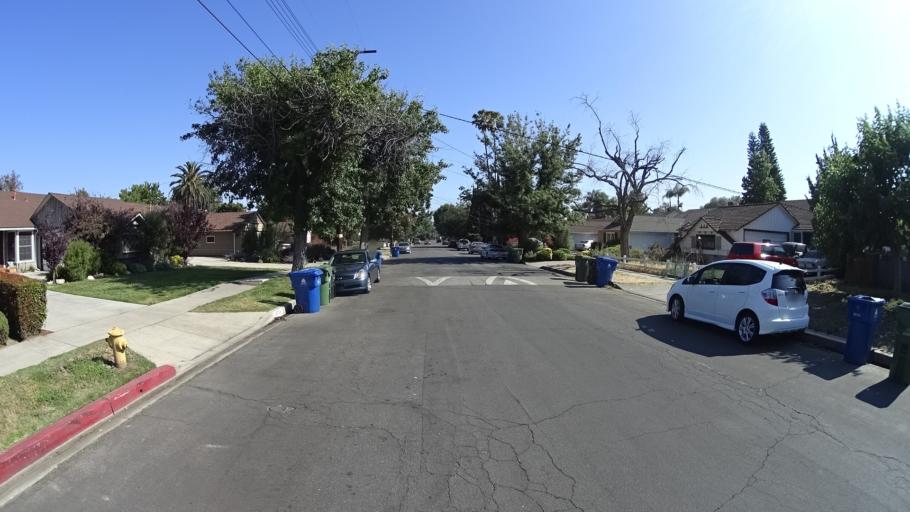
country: US
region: California
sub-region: Los Angeles County
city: Van Nuys
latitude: 34.1924
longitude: -118.4269
